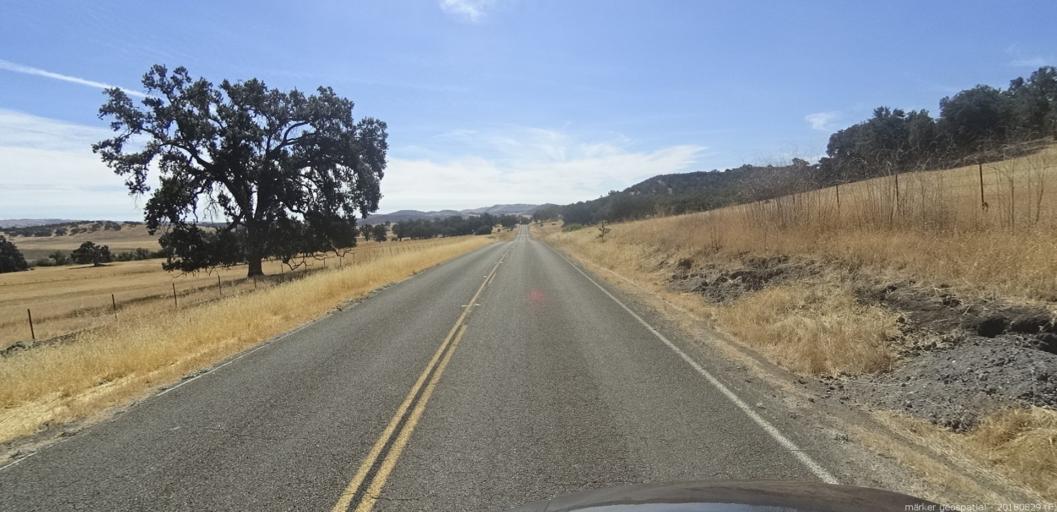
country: US
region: California
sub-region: San Luis Obispo County
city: Lake Nacimiento
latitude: 35.8250
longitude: -121.0156
